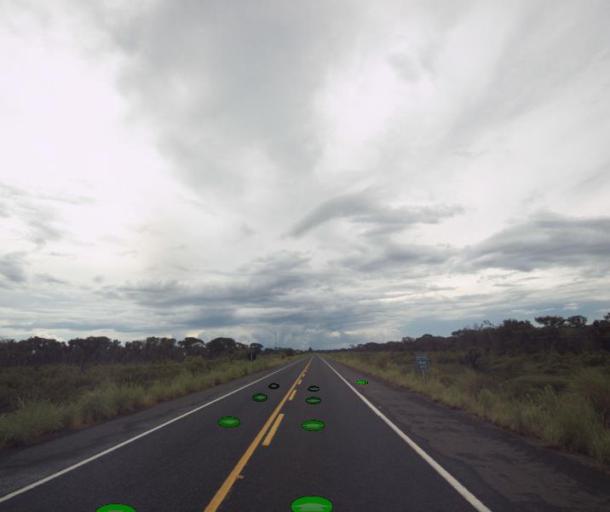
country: BR
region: Goias
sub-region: Sao Miguel Do Araguaia
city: Sao Miguel do Araguaia
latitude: -13.2302
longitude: -50.5664
